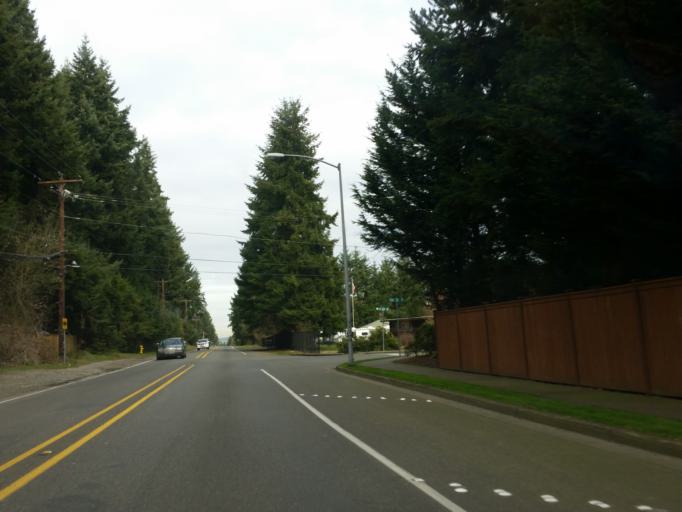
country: US
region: Washington
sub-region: Pierce County
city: South Hill
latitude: 47.1597
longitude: -122.2562
